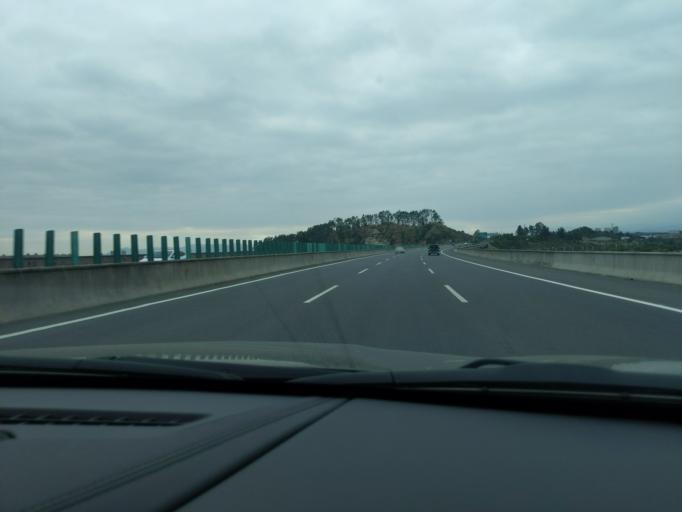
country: CN
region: Fujian
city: Neikeng
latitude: 24.7838
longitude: 118.4901
